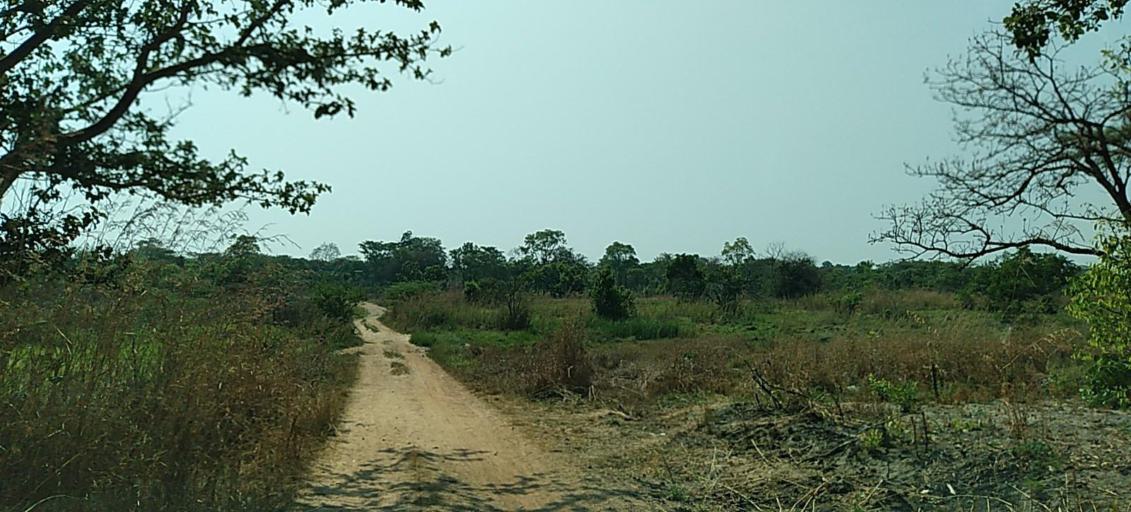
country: ZM
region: Copperbelt
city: Luanshya
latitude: -13.2807
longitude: 28.3127
